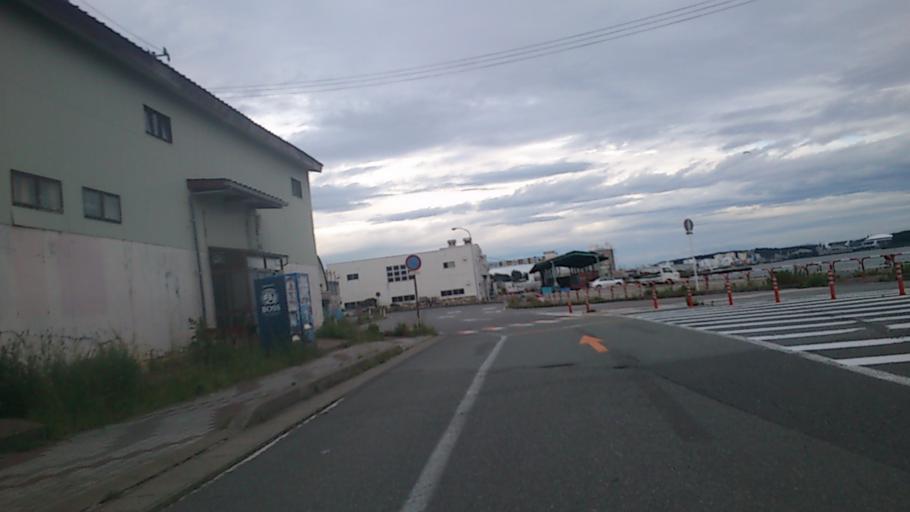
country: JP
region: Akita
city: Akita Shi
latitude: 39.7517
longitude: 140.0623
